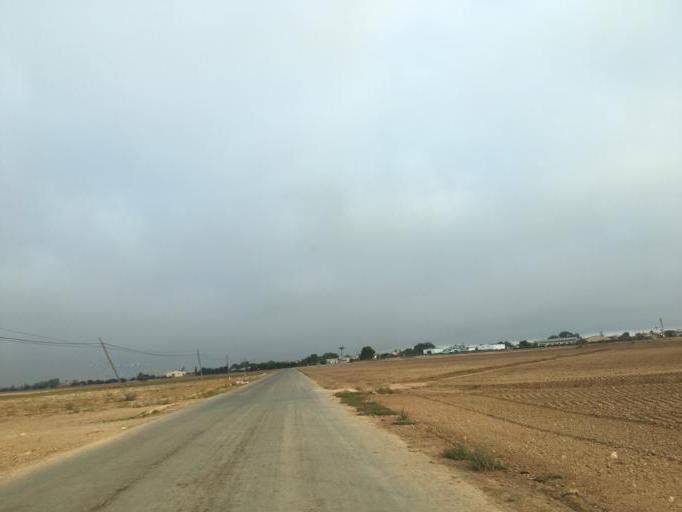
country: ES
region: Murcia
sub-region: Murcia
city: Cartagena
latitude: 37.6628
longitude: -0.9455
